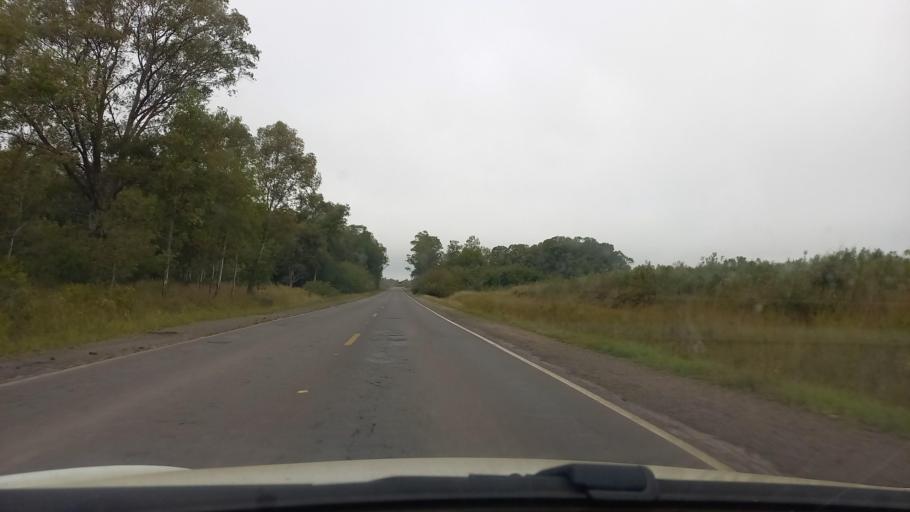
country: BR
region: Rio Grande do Sul
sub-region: Rosario Do Sul
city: Rosario do Sul
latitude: -30.1587
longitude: -54.6808
